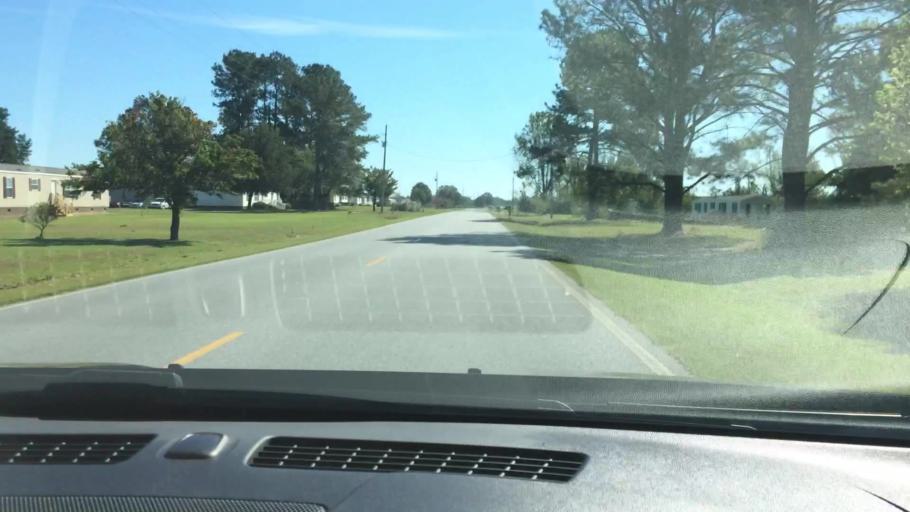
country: US
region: North Carolina
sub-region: Pitt County
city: Grifton
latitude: 35.3880
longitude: -77.3831
